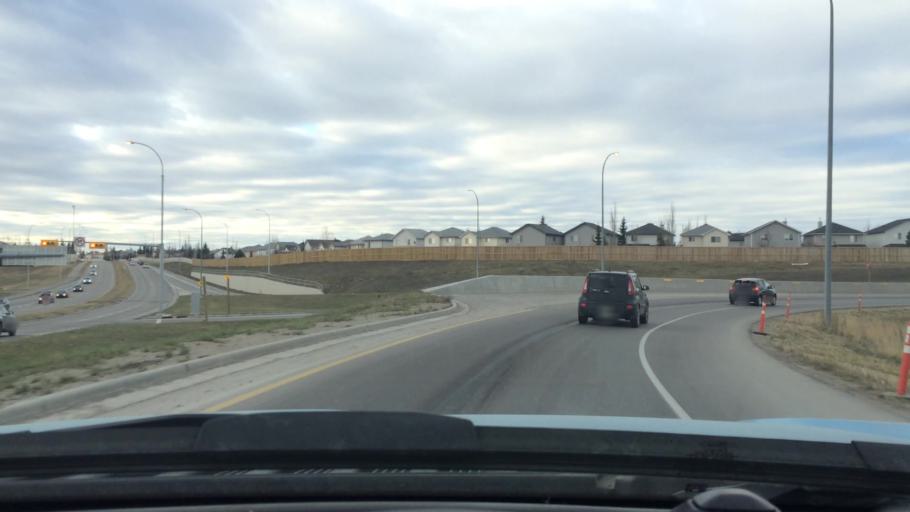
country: CA
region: Alberta
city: Calgary
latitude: 51.1503
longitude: -114.1670
